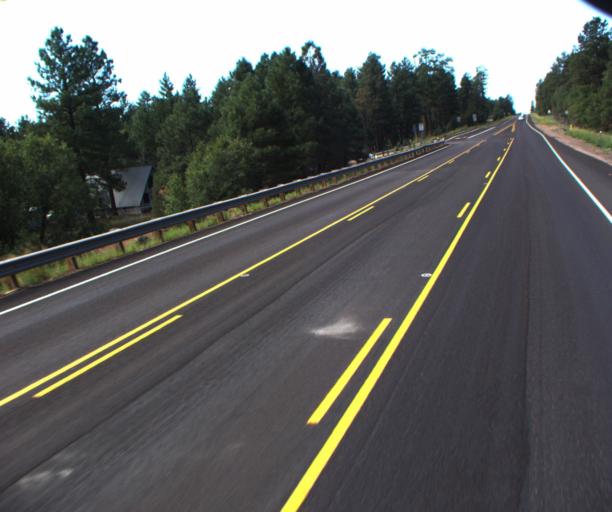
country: US
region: Arizona
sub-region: Navajo County
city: Show Low
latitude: 34.2104
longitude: -110.0766
